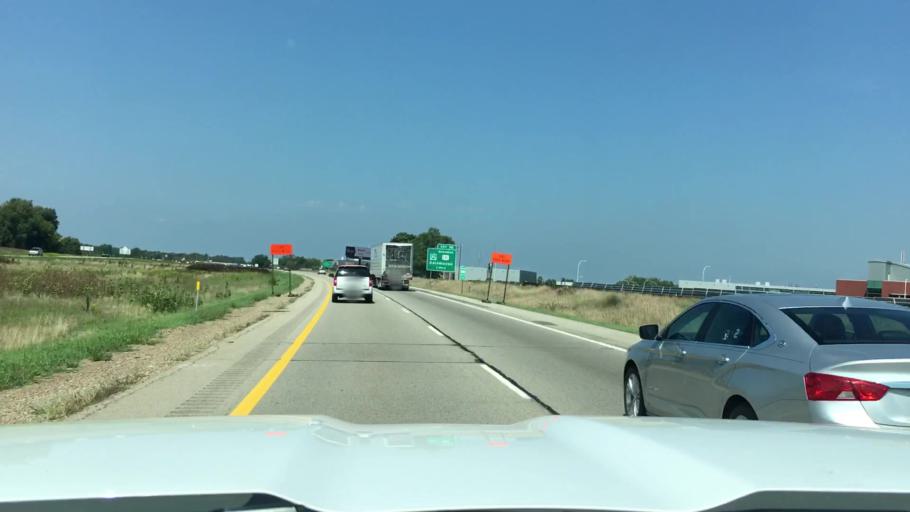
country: US
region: Michigan
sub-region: Kalamazoo County
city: Westwood
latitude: 42.2498
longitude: -85.6421
